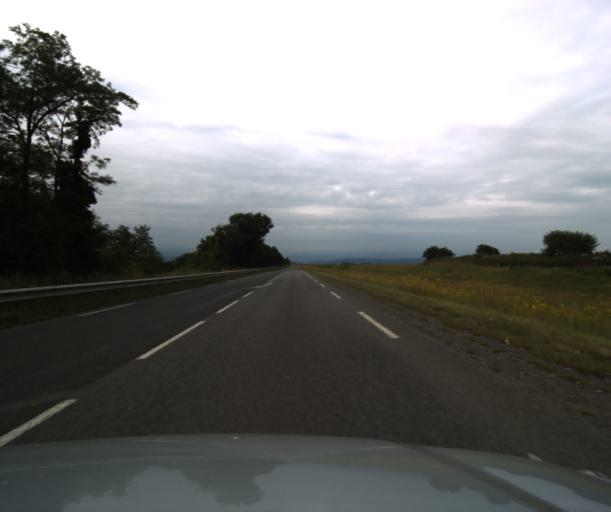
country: FR
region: Midi-Pyrenees
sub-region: Departement des Hautes-Pyrenees
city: Juillan
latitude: 43.2162
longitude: 0.0152
